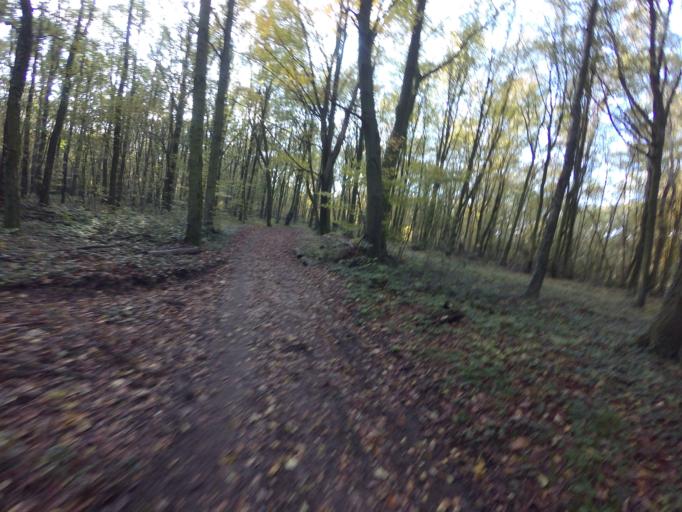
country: BE
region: Wallonia
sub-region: Province de Liege
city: Plombieres
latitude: 50.7748
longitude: 5.9701
